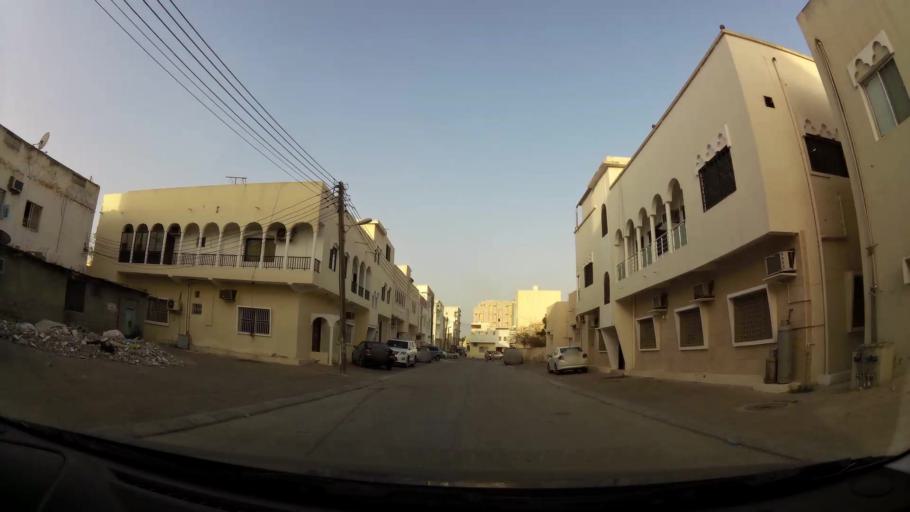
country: OM
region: Zufar
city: Salalah
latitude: 17.0144
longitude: 54.1076
